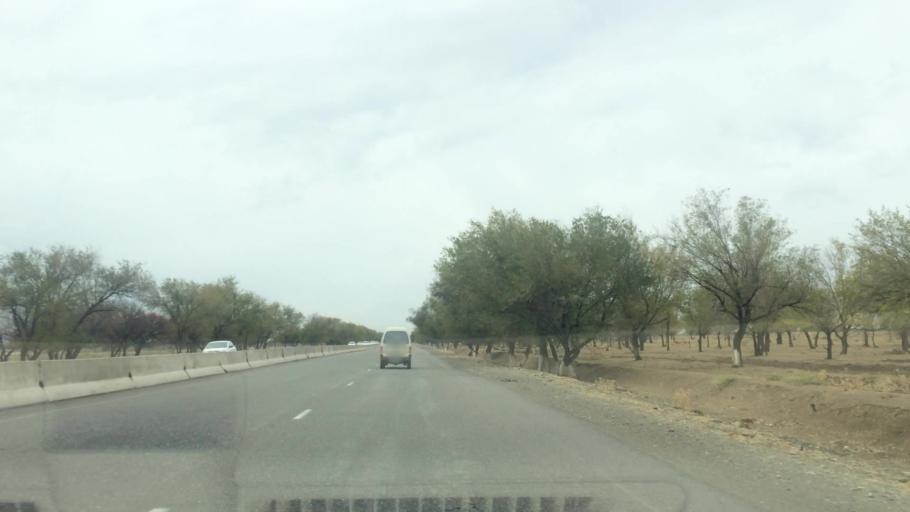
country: UZ
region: Samarqand
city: Bulung'ur
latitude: 39.8139
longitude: 67.3737
